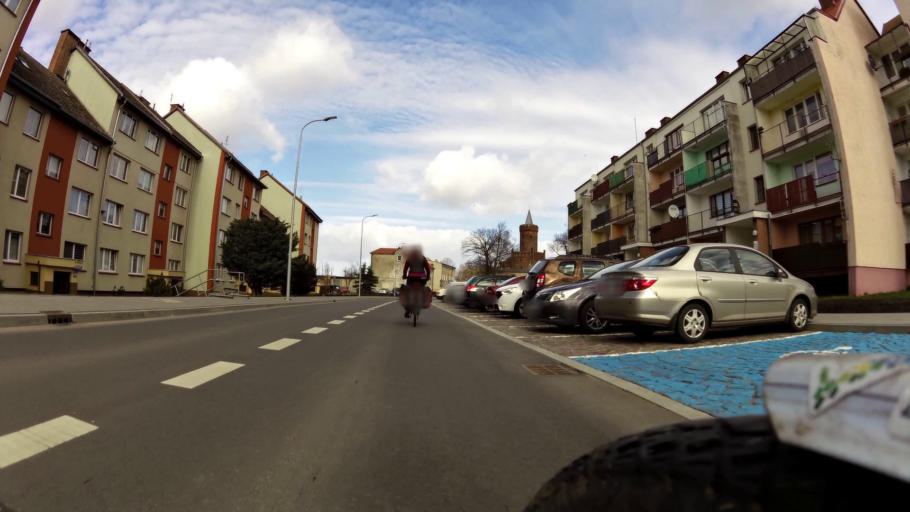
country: PL
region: West Pomeranian Voivodeship
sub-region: Powiat kamienski
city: Kamien Pomorski
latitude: 53.9704
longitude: 14.7657
